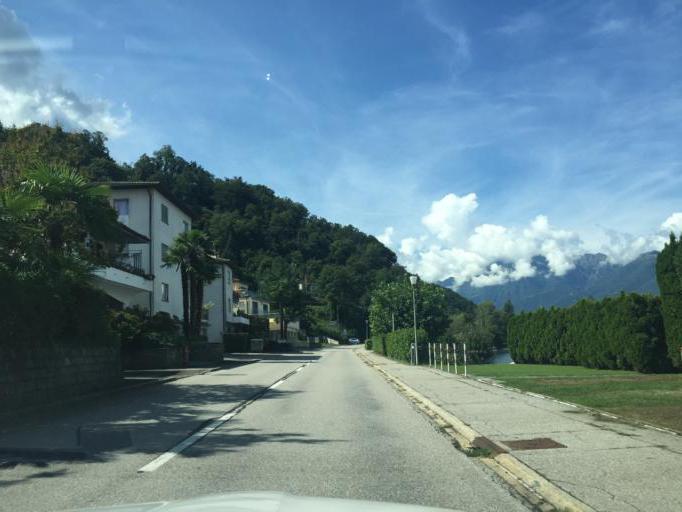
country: CH
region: Ticino
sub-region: Locarno District
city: Magadino
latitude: 46.1415
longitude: 8.8366
